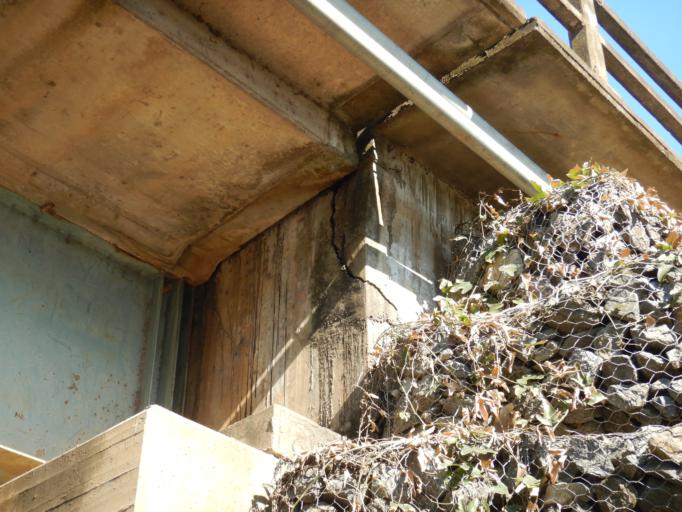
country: AR
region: Entre Rios
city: Parana
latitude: -31.6712
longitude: -60.5796
